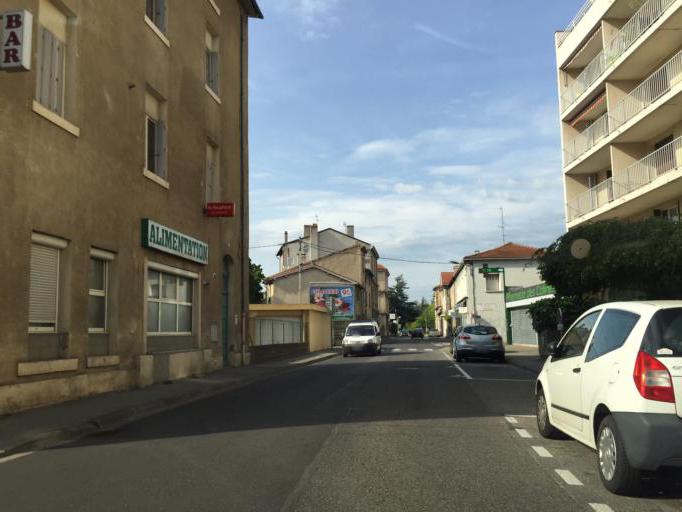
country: FR
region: Rhone-Alpes
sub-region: Departement de la Drome
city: Romans-sur-Isere
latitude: 45.0516
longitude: 5.0477
